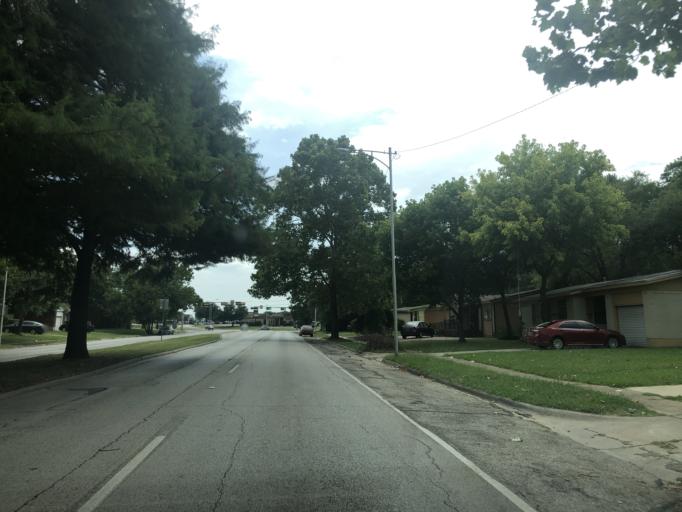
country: US
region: Texas
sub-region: Dallas County
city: Grand Prairie
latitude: 32.7501
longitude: -97.0174
